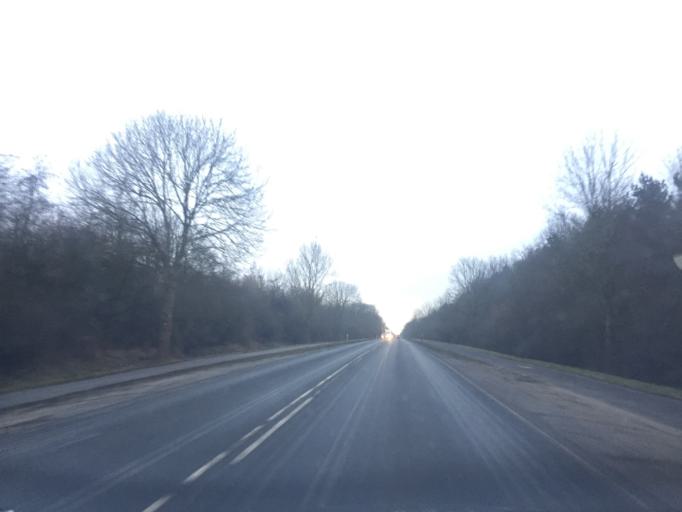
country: DK
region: Zealand
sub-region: Solrod Kommune
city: Solrod Strand
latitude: 55.5491
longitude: 12.2154
